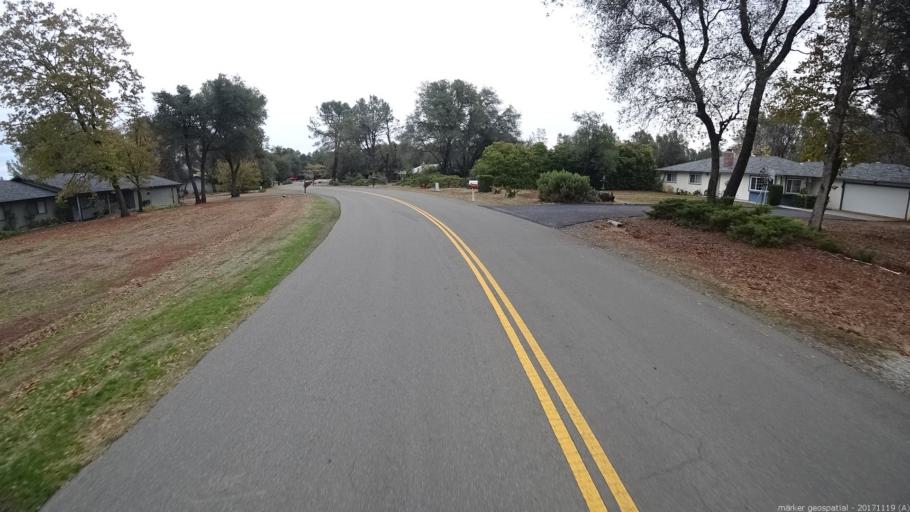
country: US
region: California
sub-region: Shasta County
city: Redding
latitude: 40.4946
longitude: -122.4133
